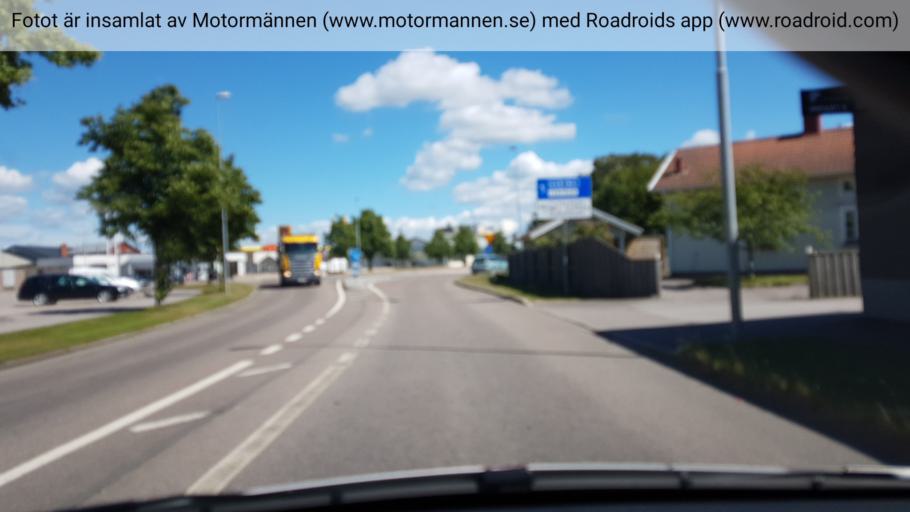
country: SE
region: Vaestra Goetaland
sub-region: Lidkopings Kommun
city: Lidkoping
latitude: 58.5083
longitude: 13.1492
